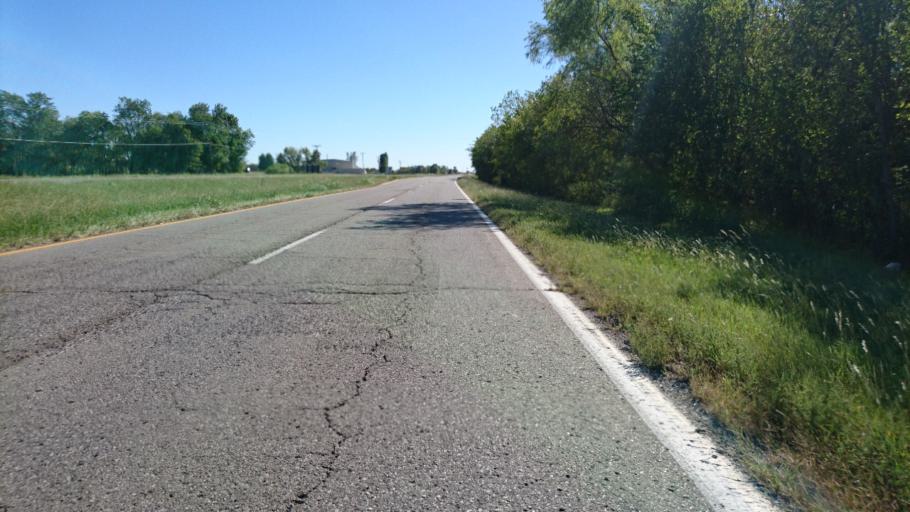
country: US
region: Oklahoma
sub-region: Rogers County
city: Bushyhead
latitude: 36.4102
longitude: -95.5393
